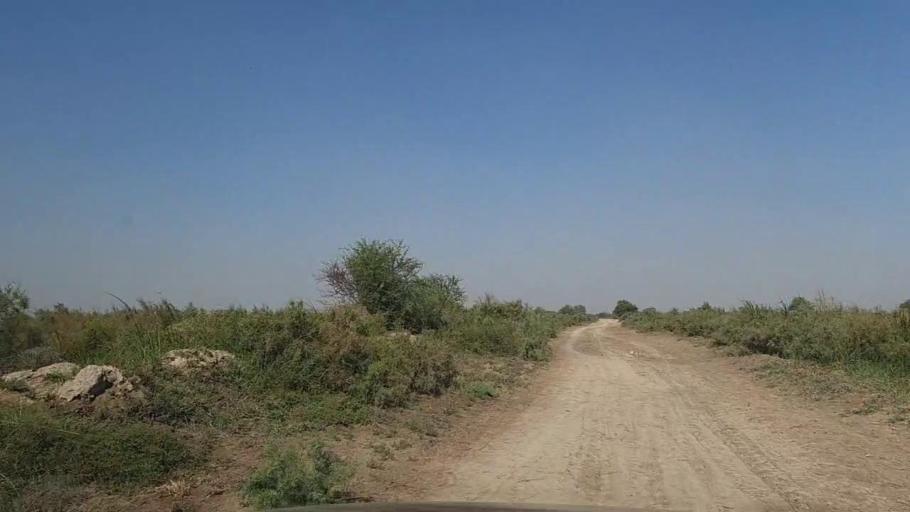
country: PK
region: Sindh
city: Daro Mehar
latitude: 24.8228
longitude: 68.1503
